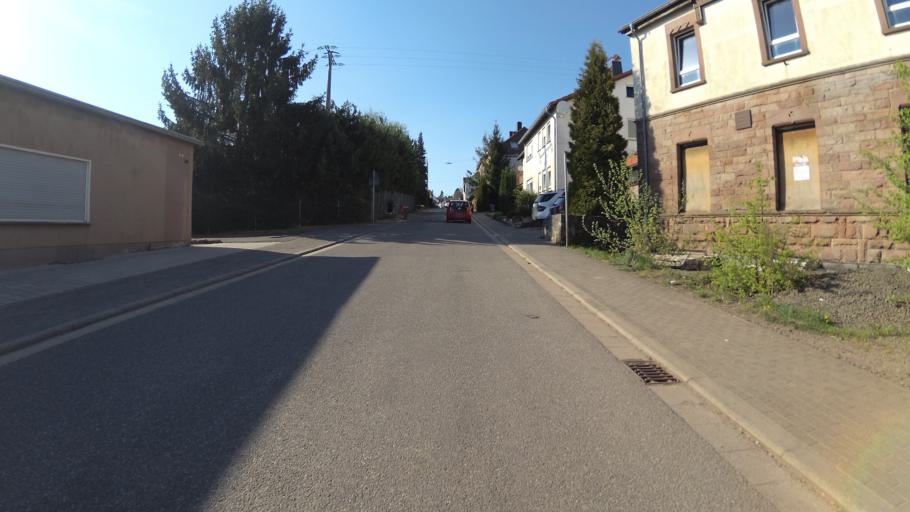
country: DE
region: Saarland
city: Merchweiler
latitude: 49.3545
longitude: 7.0638
